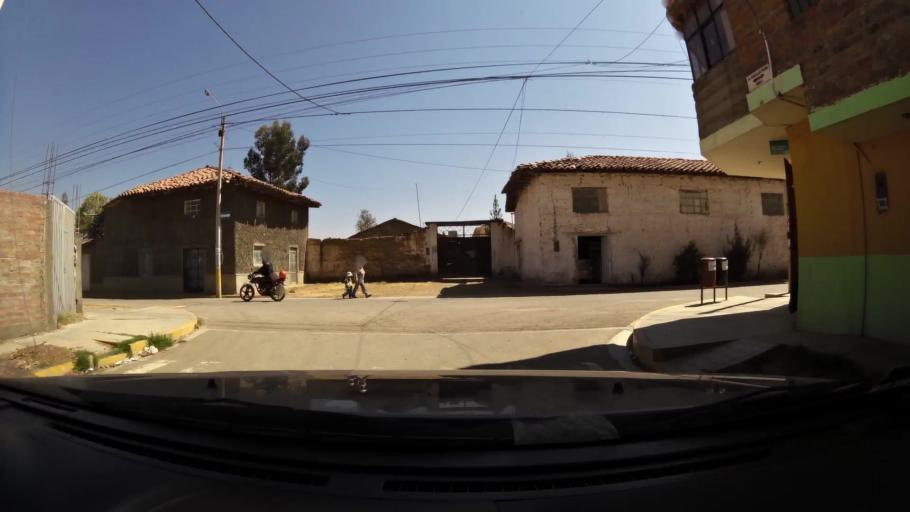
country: PE
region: Junin
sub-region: Provincia de Concepcion
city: Concepcion
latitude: -11.9148
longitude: -75.3179
